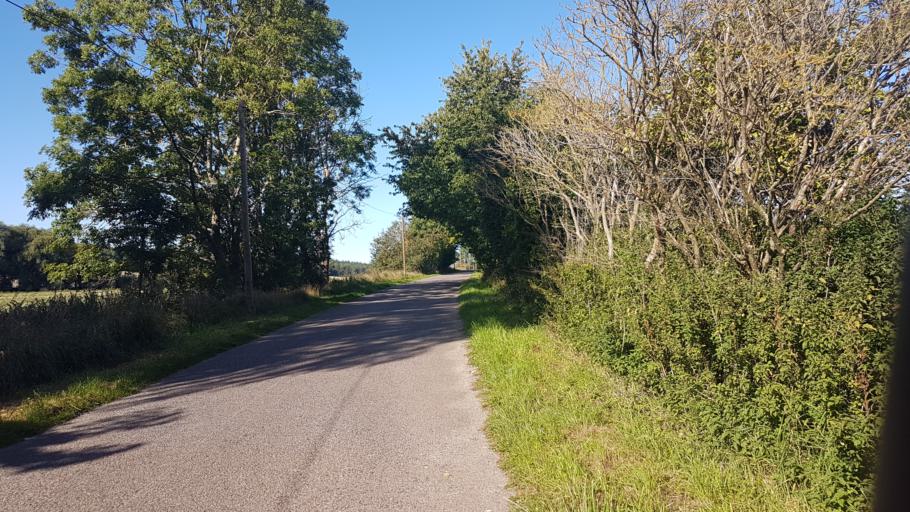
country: DE
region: Mecklenburg-Vorpommern
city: Sagard
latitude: 54.5040
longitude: 13.5288
